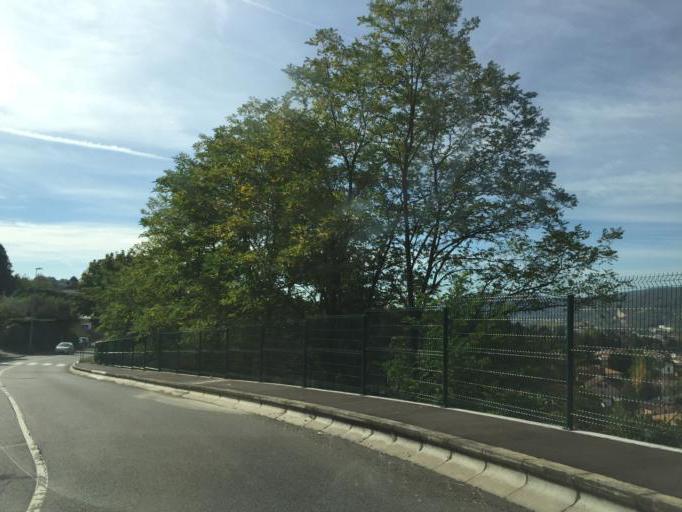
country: FR
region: Rhone-Alpes
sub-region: Departement du Rhone
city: Neuville-sur-Saone
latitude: 45.8816
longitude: 4.8537
